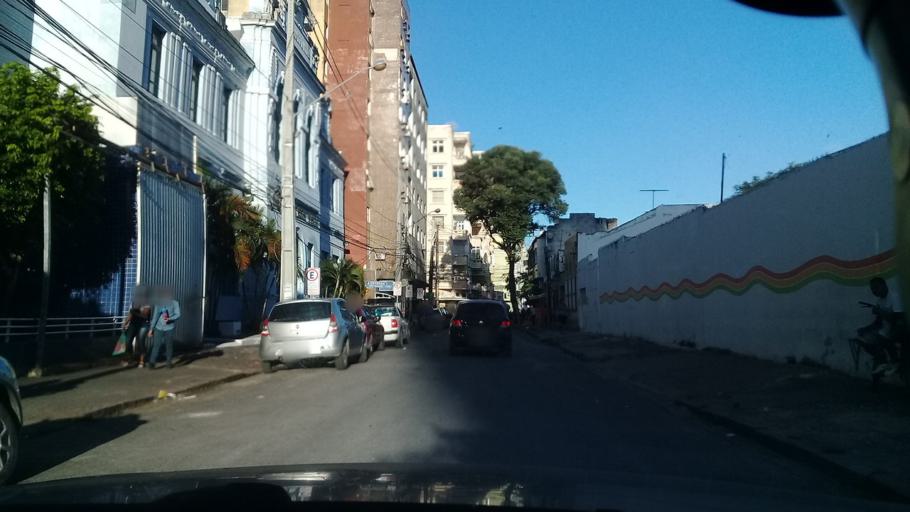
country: BR
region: Pernambuco
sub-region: Recife
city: Recife
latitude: -8.0600
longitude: -34.8878
